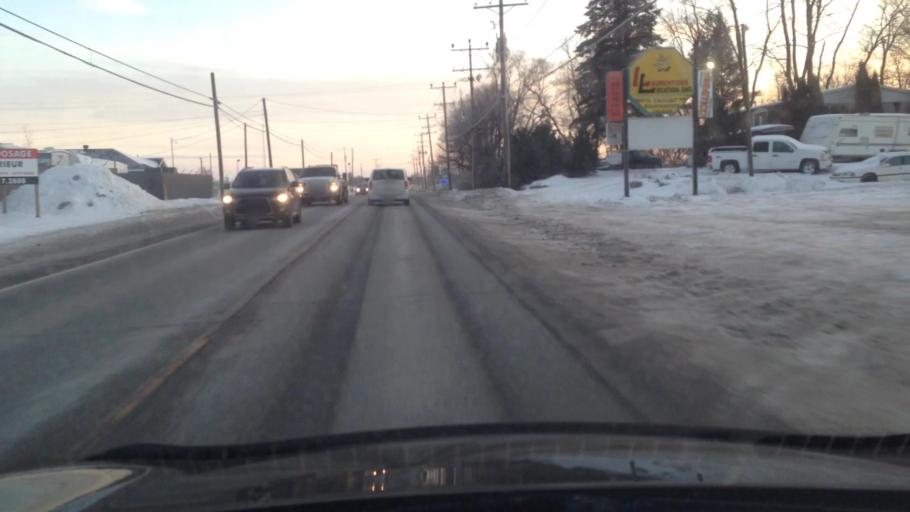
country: CA
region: Quebec
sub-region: Lanaudiere
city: Saint-Lin-Laurentides
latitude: 45.8875
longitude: -73.7580
